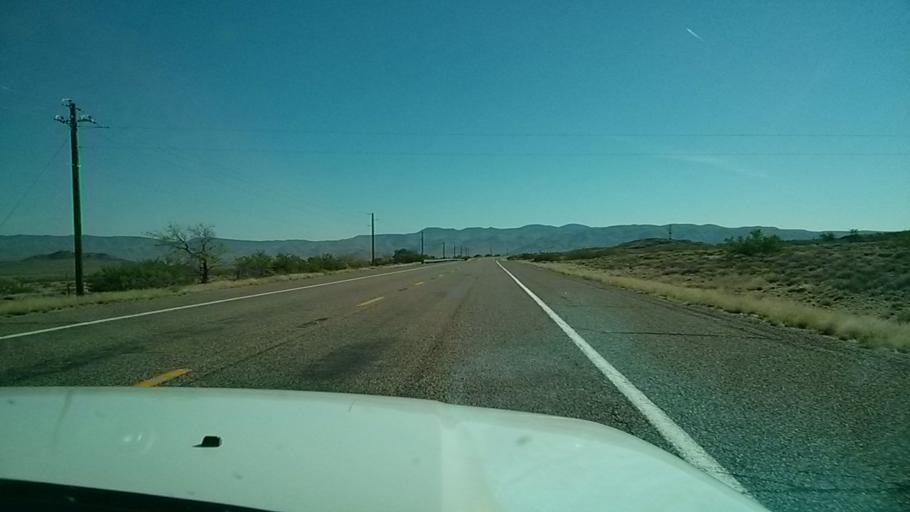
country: US
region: Arizona
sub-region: Mohave County
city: New Kingman-Butler
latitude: 35.4075
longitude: -113.8284
